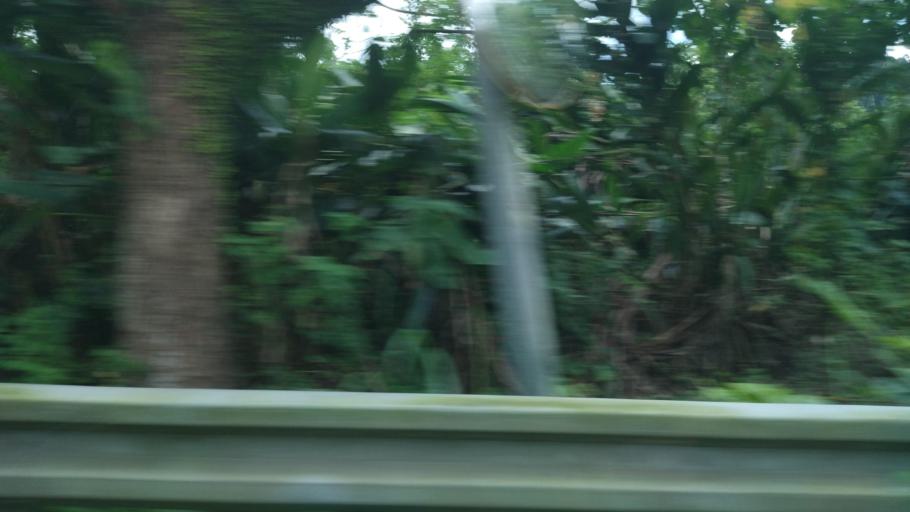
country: TW
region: Taipei
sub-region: Taipei
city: Banqiao
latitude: 24.9295
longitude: 121.4507
